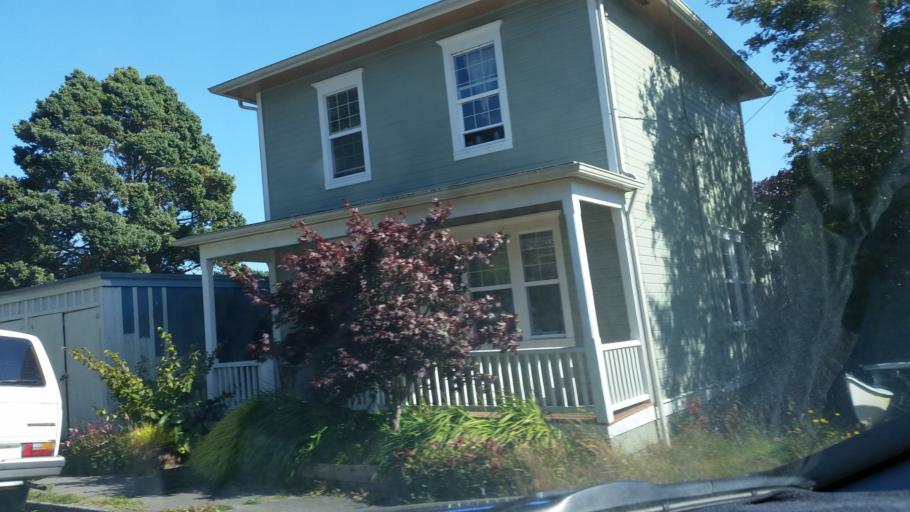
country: US
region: Oregon
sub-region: Clatsop County
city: Astoria
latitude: 46.1828
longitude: -123.8389
